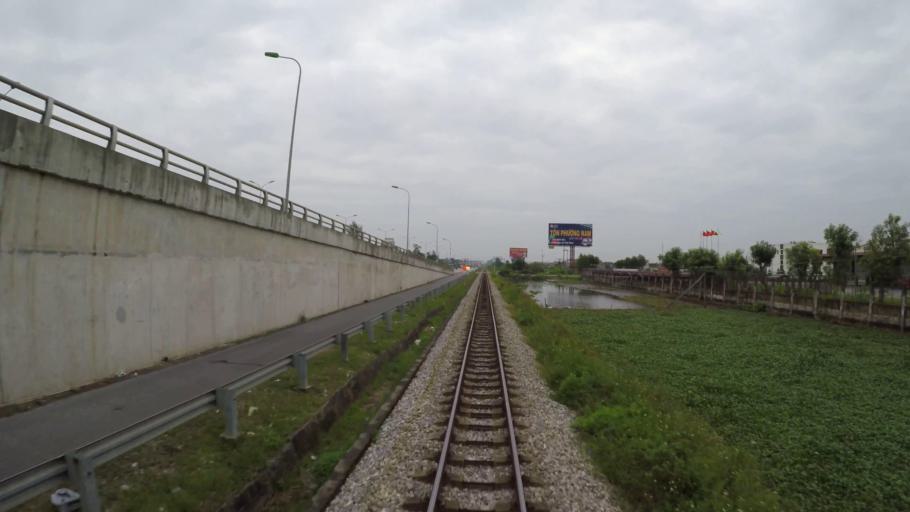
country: VN
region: Hai Duong
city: Nam Sach
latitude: 20.9655
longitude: 106.3764
